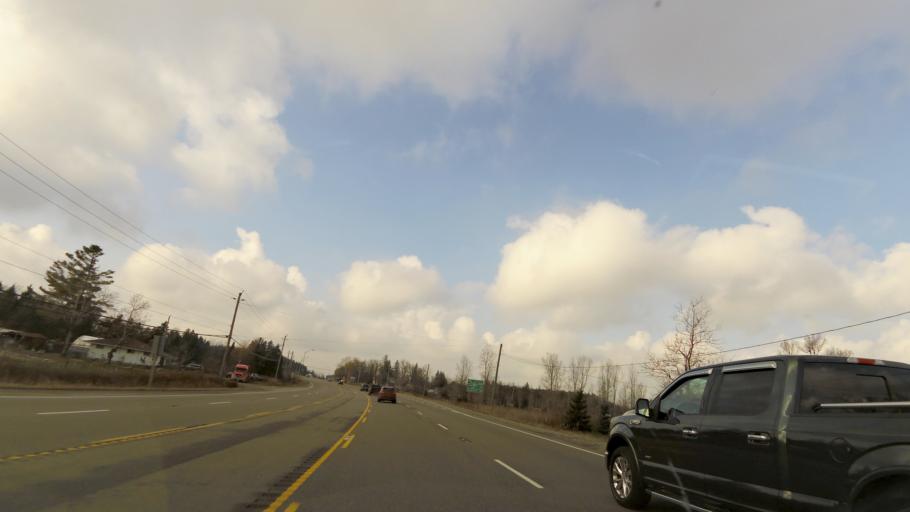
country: CA
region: Ontario
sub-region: Halton
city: Milton
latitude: 43.4181
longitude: -80.0628
